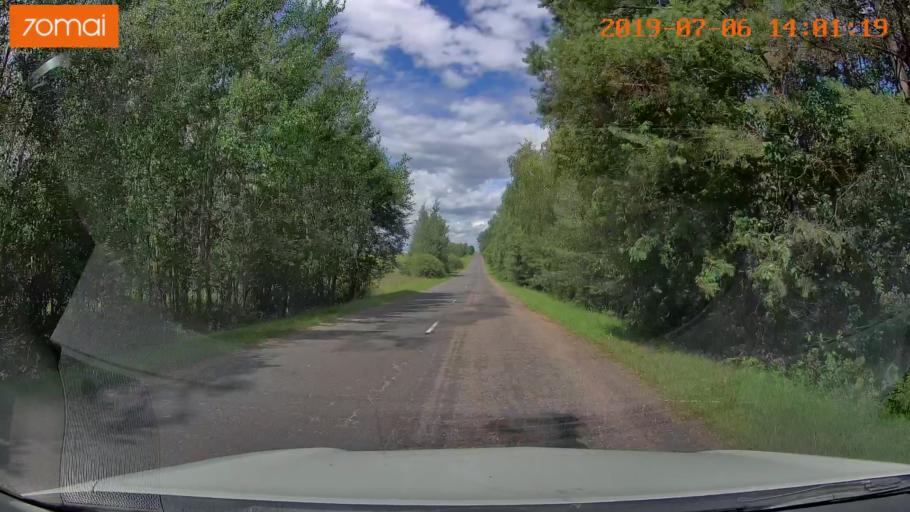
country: BY
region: Minsk
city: Ivyanyets
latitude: 53.8067
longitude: 26.8138
